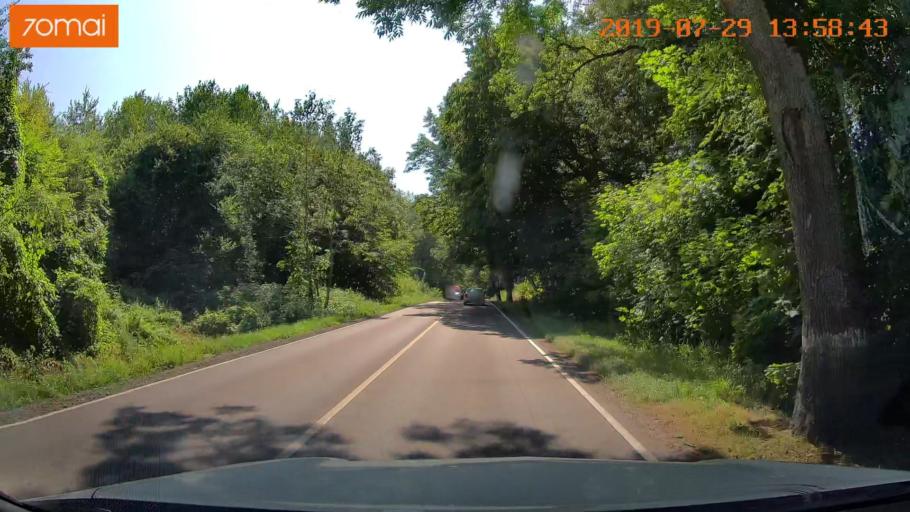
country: RU
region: Kaliningrad
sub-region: Gorod Kaliningrad
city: Baltiysk
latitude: 54.6909
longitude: 19.9357
